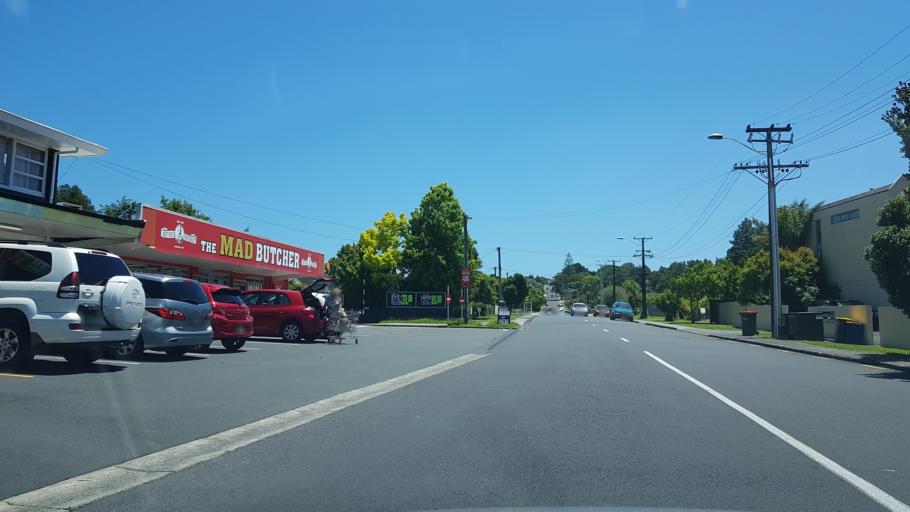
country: NZ
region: Auckland
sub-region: Auckland
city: North Shore
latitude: -36.7948
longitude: 174.7443
